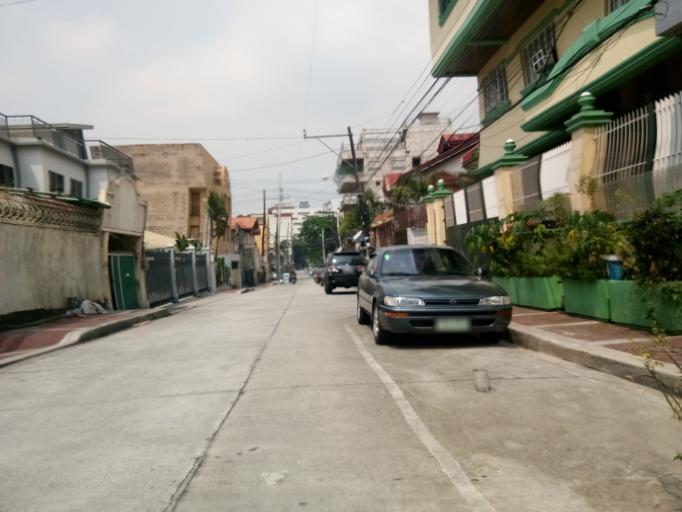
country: PH
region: Metro Manila
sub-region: Pasig
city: Pasig City
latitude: 14.6146
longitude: 121.0585
